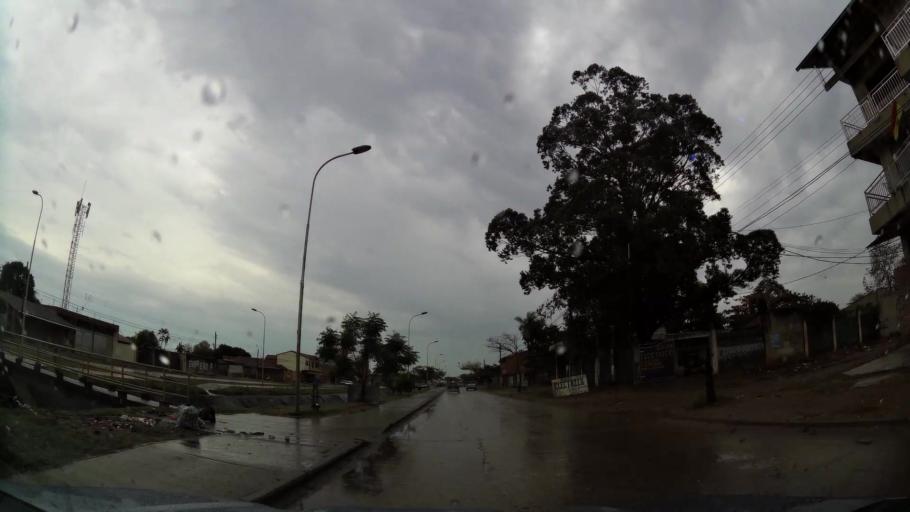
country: BO
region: Santa Cruz
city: Santa Cruz de la Sierra
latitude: -17.8118
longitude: -63.1311
